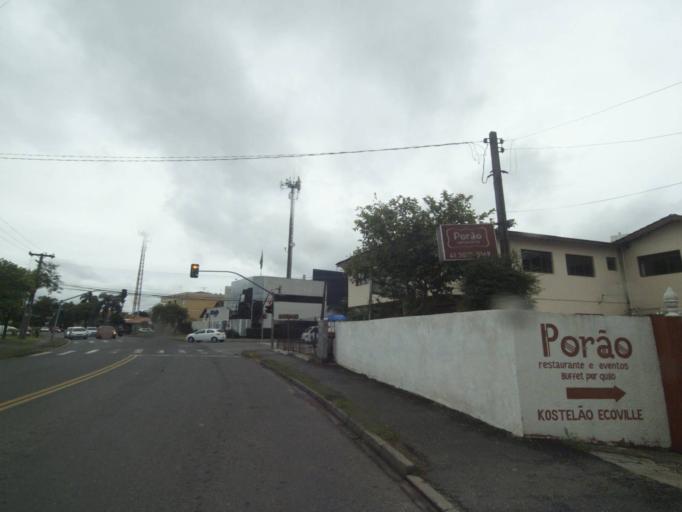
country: BR
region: Parana
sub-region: Curitiba
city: Curitiba
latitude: -25.4440
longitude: -49.3432
